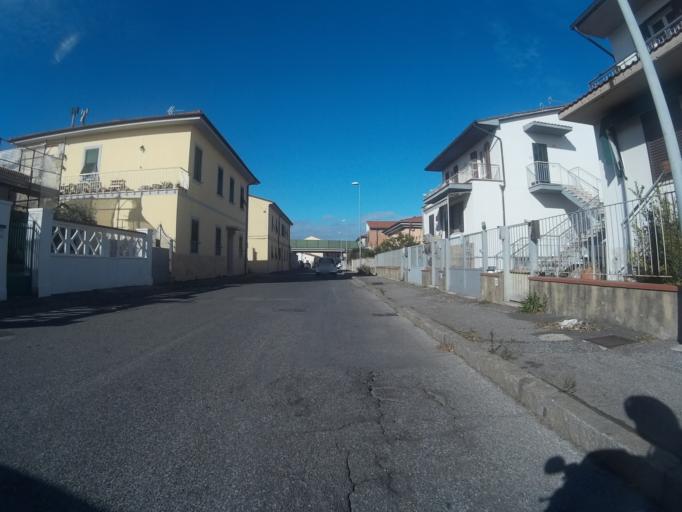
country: IT
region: Tuscany
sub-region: Provincia di Livorno
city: Livorno
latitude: 43.5412
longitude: 10.3396
